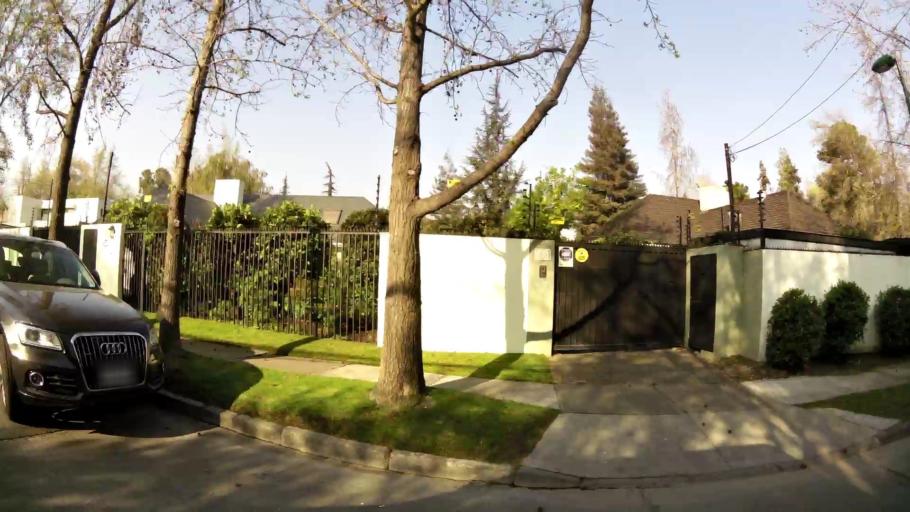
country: CL
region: Santiago Metropolitan
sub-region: Provincia de Santiago
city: Villa Presidente Frei, Nunoa, Santiago, Chile
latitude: -33.3621
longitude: -70.5316
